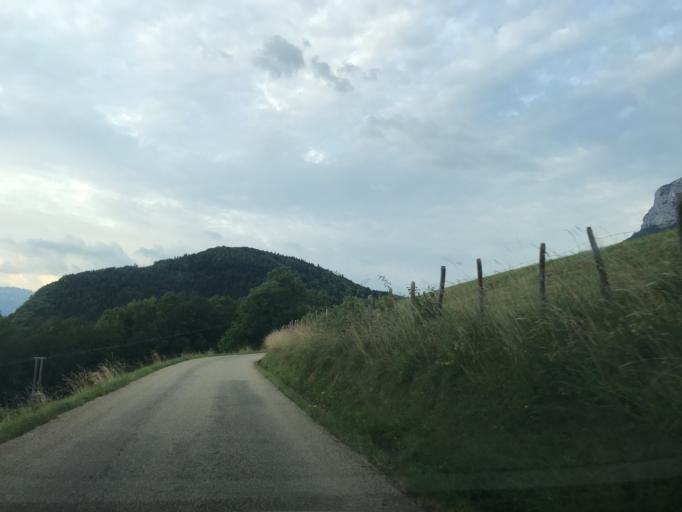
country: FR
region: Rhone-Alpes
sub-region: Departement de l'Isere
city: Saint-Vincent-de-Mercuze
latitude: 45.3939
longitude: 5.9371
